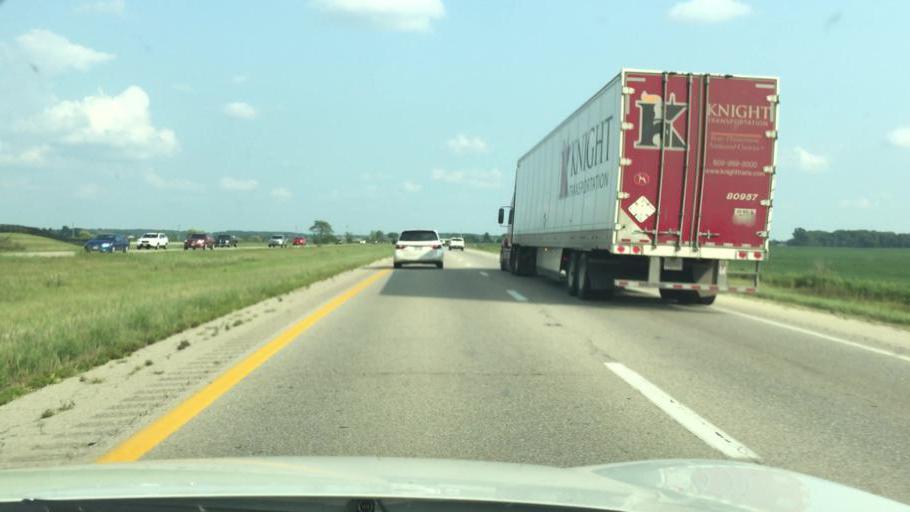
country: US
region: Ohio
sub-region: Union County
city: New California
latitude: 40.1940
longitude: -83.2717
